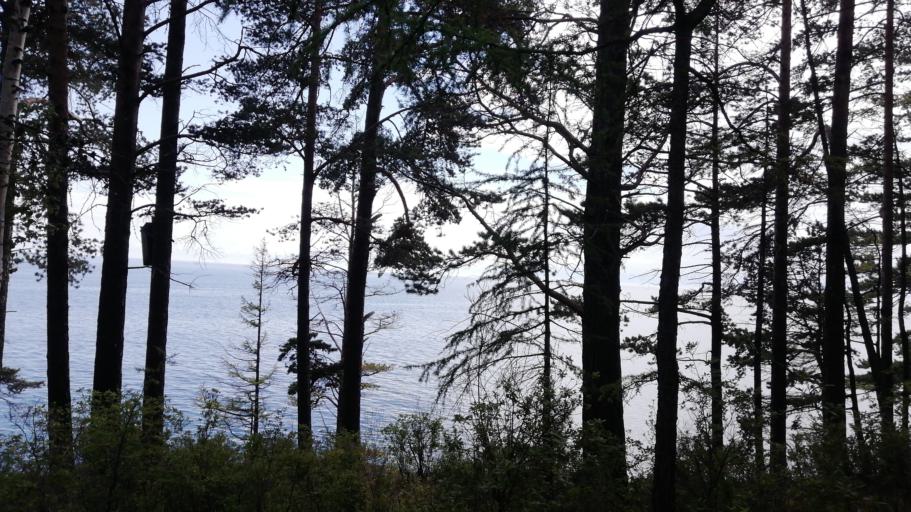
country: RU
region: Irkutsk
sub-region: Irkutskiy Rayon
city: Listvyanka
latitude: 51.8945
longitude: 105.0514
